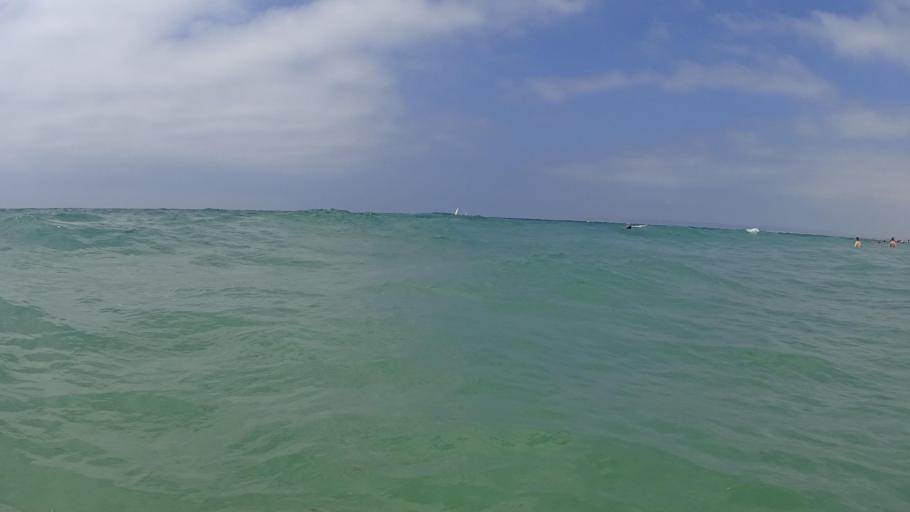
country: ES
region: Andalusia
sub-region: Provincia de Cadiz
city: Zahara de los Atunes
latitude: 36.1065
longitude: -5.8273
